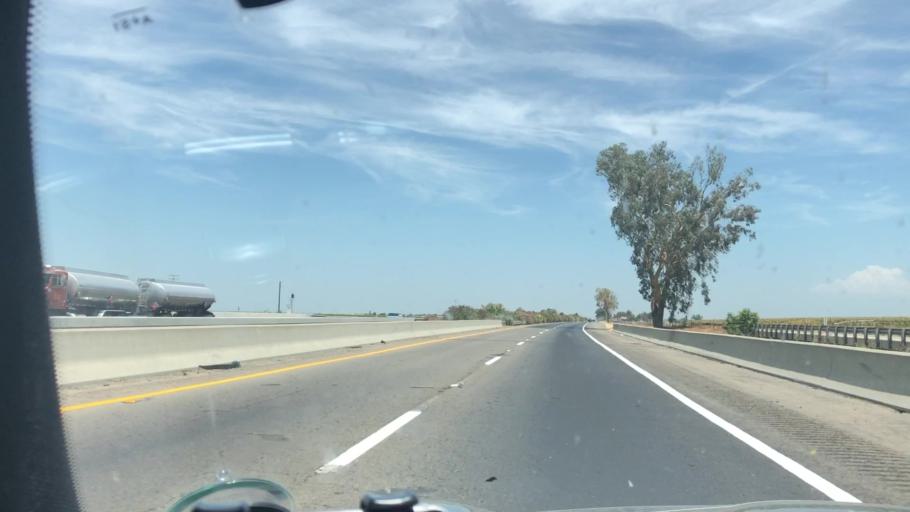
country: US
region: California
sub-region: Tulare County
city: Tipton
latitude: 36.0936
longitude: -119.3219
